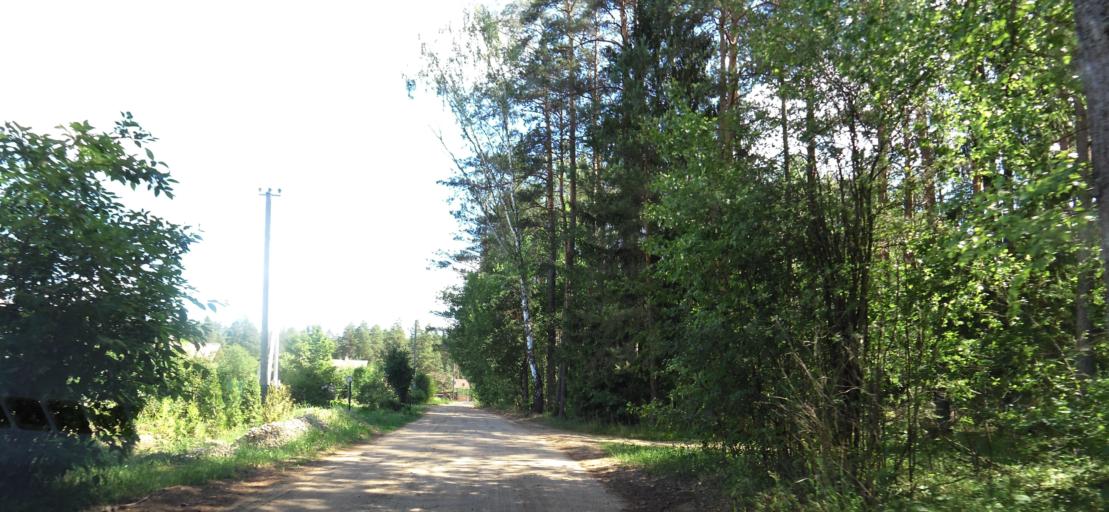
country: LT
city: Nemencine
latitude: 54.8241
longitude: 25.4106
